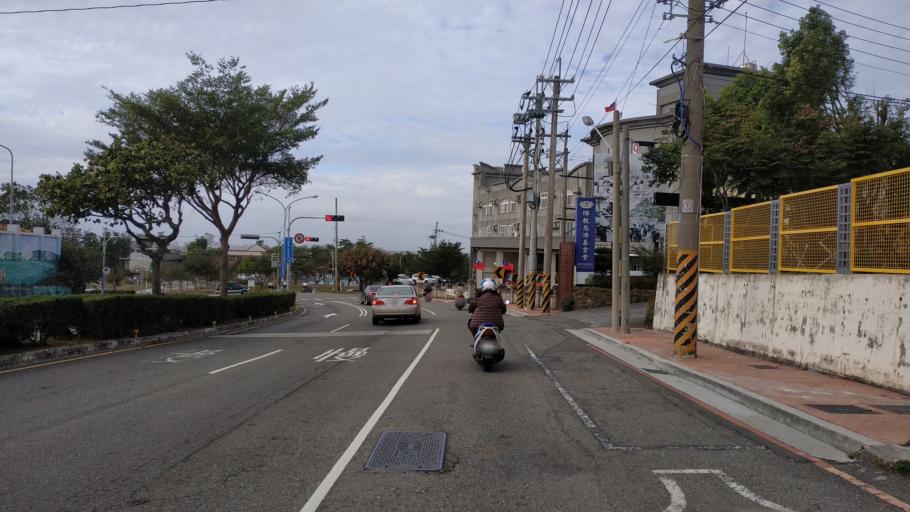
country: TW
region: Taiwan
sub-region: Taichung City
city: Taichung
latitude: 24.2319
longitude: 120.5658
